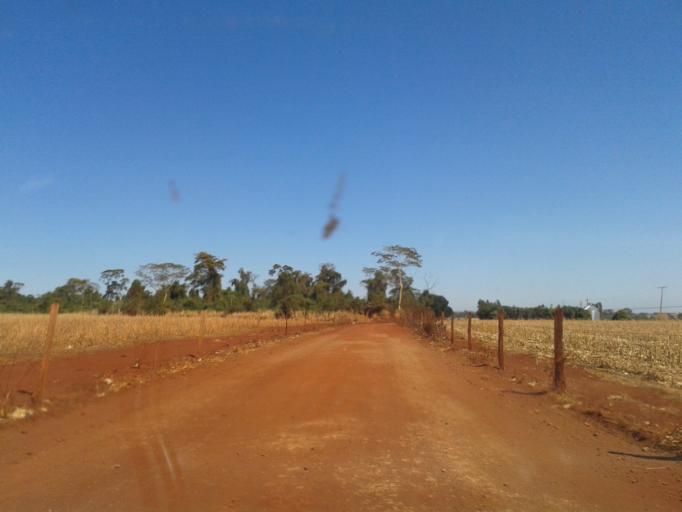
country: BR
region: Minas Gerais
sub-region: Centralina
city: Centralina
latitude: -18.5851
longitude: -49.1384
